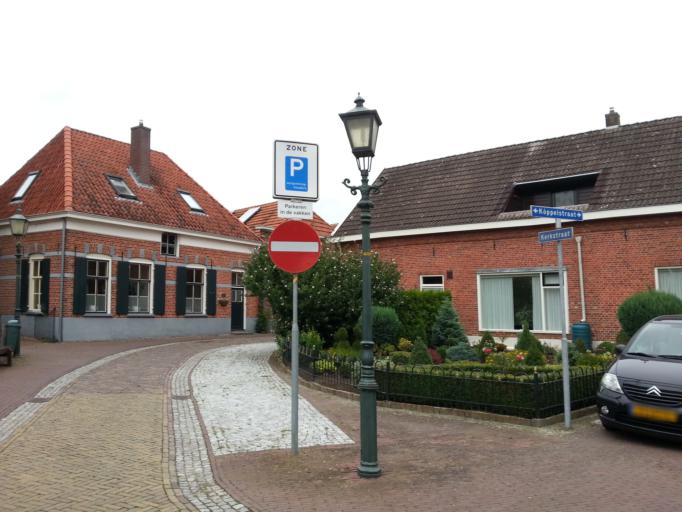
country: NL
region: Gelderland
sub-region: Gemeente Aalten
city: Bredevoort
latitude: 51.9422
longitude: 6.6163
